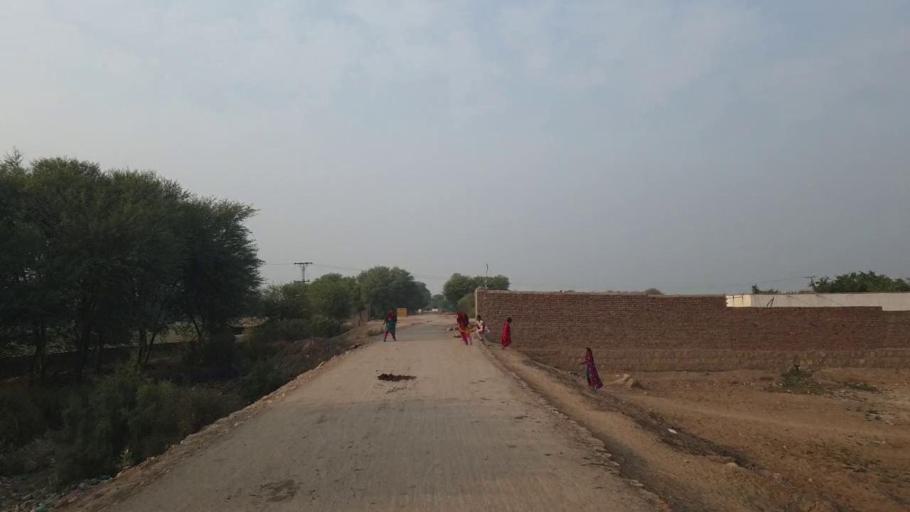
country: PK
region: Sindh
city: Sann
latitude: 26.1393
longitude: 68.0505
